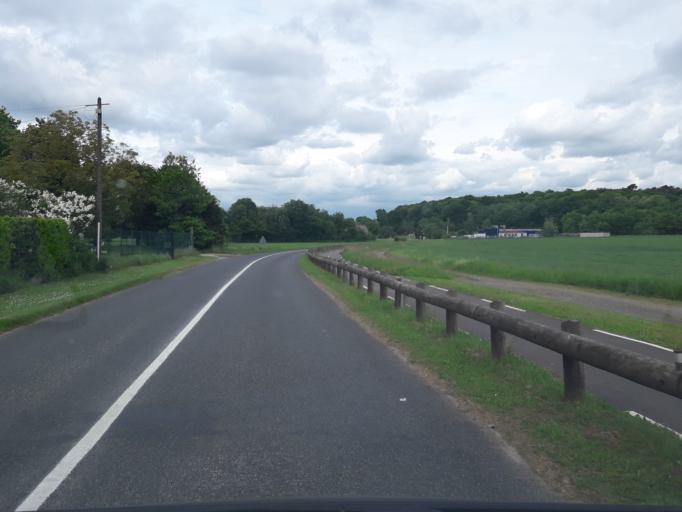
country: FR
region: Ile-de-France
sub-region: Departement de l'Essonne
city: Cerny
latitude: 48.4517
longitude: 2.3100
